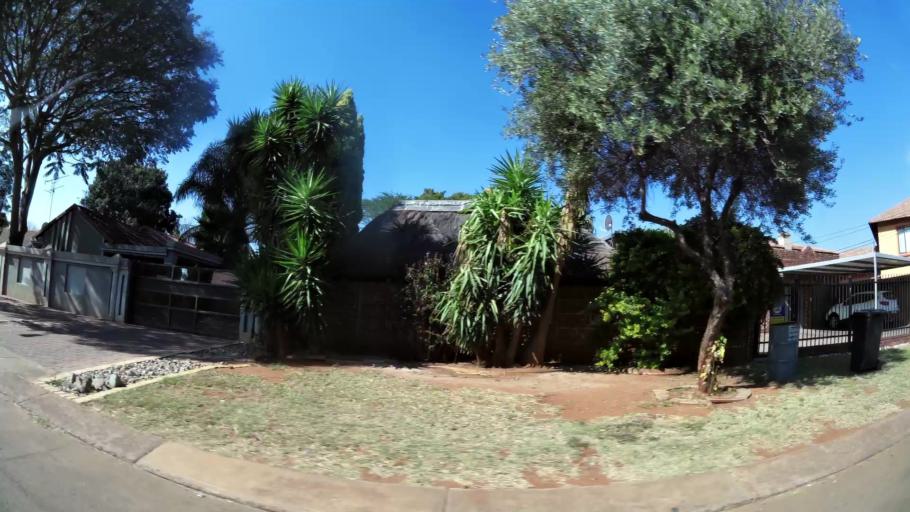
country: ZA
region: Gauteng
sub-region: City of Tshwane Metropolitan Municipality
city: Pretoria
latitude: -25.6586
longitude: 28.2505
